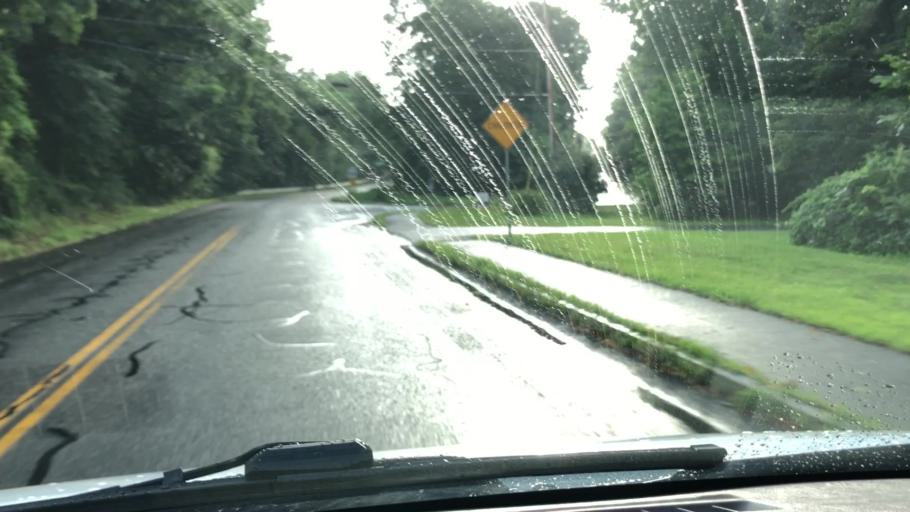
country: US
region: Massachusetts
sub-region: Hampshire County
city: Northampton
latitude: 42.3073
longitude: -72.6551
